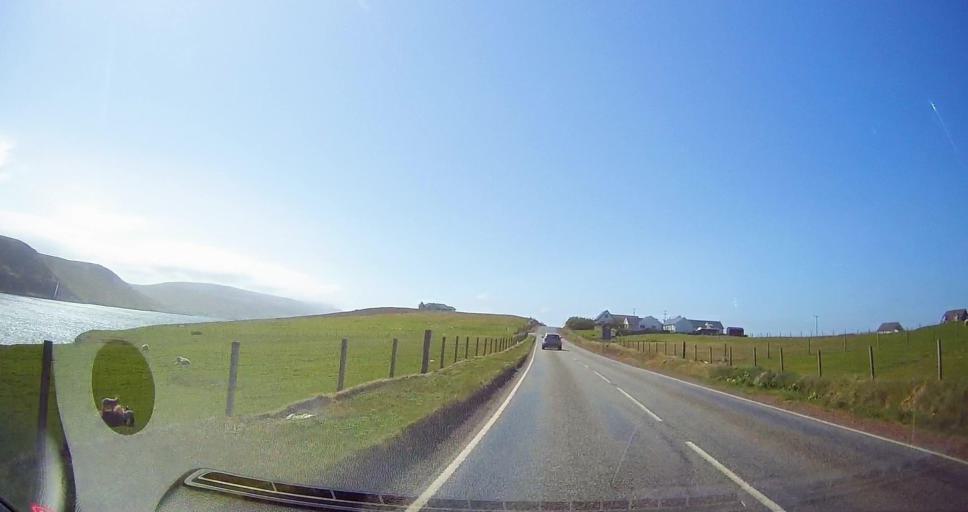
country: GB
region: Scotland
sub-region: Shetland Islands
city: Sandwick
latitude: 60.1248
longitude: -1.2845
